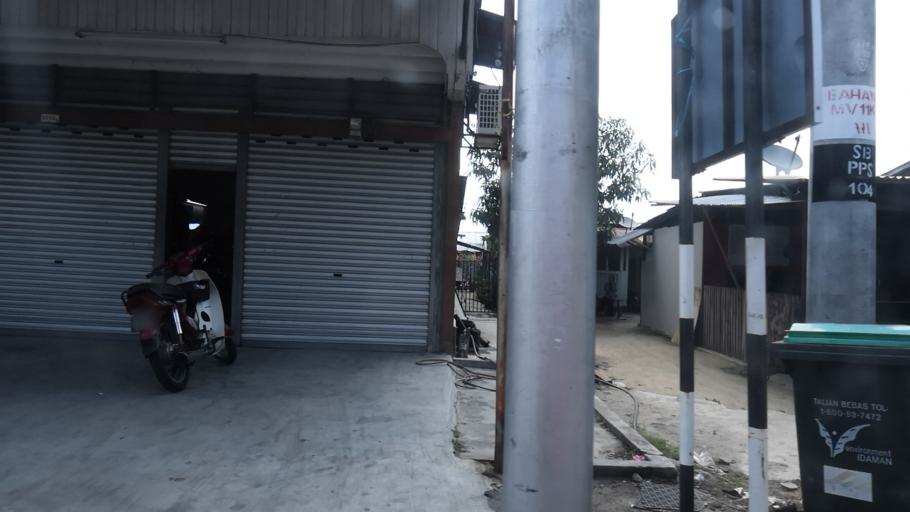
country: MY
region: Perak
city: Lumut
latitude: 4.2194
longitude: 100.5749
